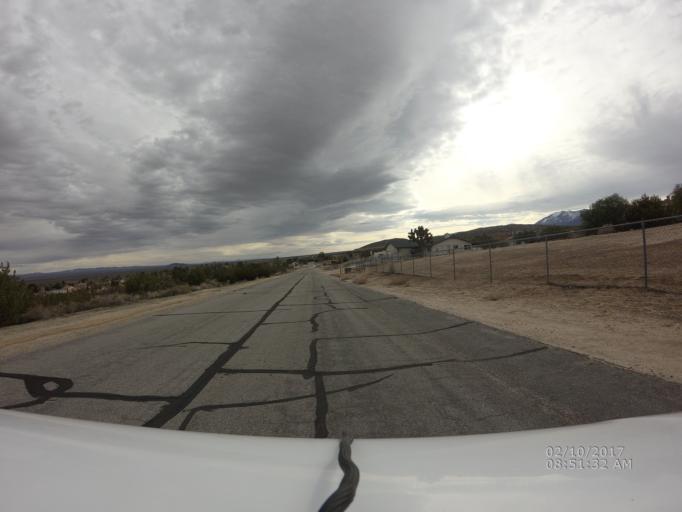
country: US
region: California
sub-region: Los Angeles County
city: Littlerock
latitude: 34.4846
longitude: -117.9026
